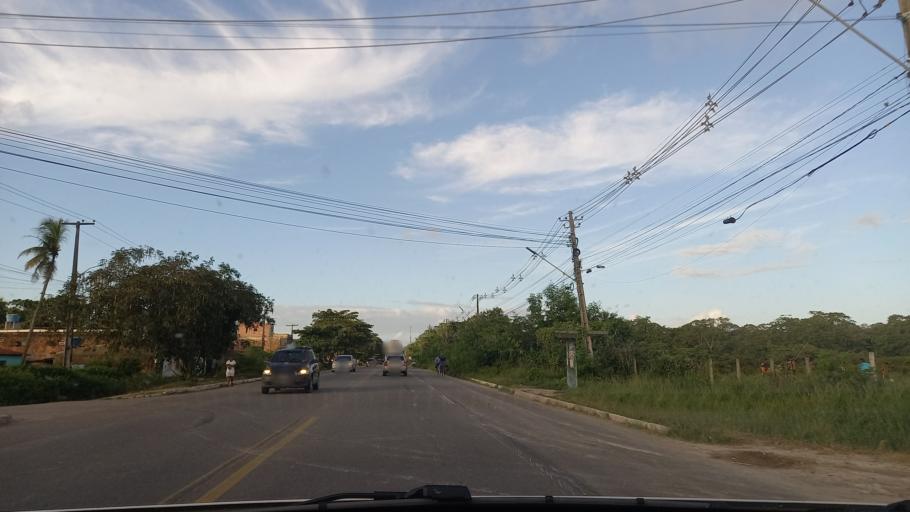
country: BR
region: Pernambuco
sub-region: Jaboatao Dos Guararapes
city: Jaboatao
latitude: -8.2325
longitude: -34.9767
